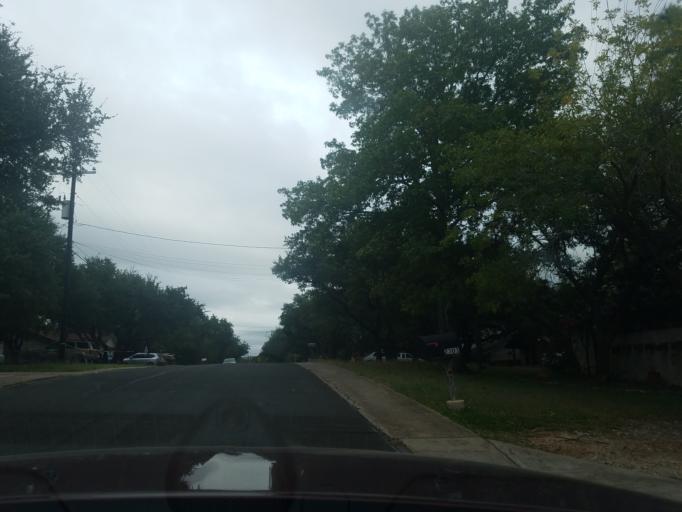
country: US
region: Texas
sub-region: Williamson County
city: Cedar Park
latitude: 30.4804
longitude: -97.8123
